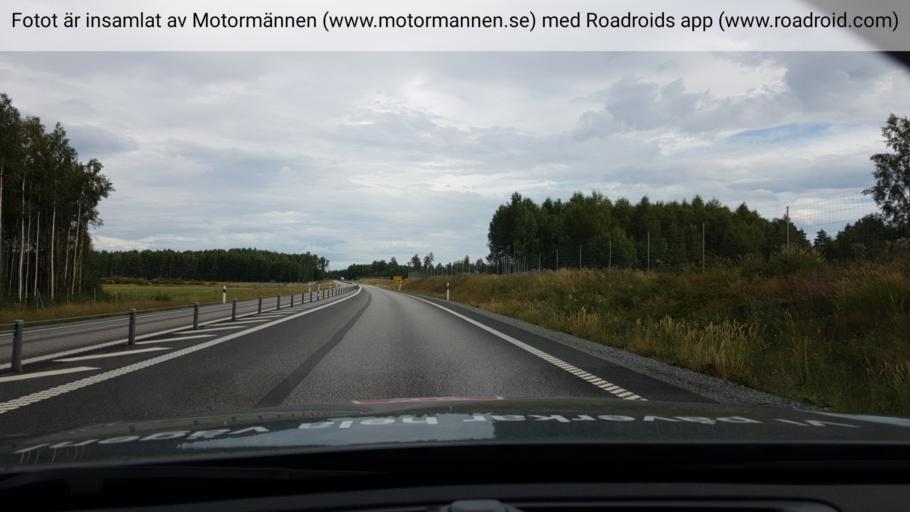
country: SE
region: Uppsala
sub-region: Heby Kommun
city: Heby
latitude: 60.0305
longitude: 16.8692
